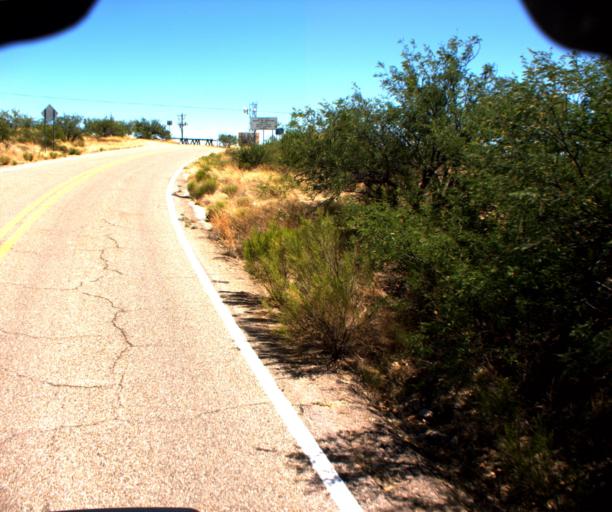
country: US
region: Arizona
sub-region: Santa Cruz County
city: Tubac
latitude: 31.4857
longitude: -111.5437
